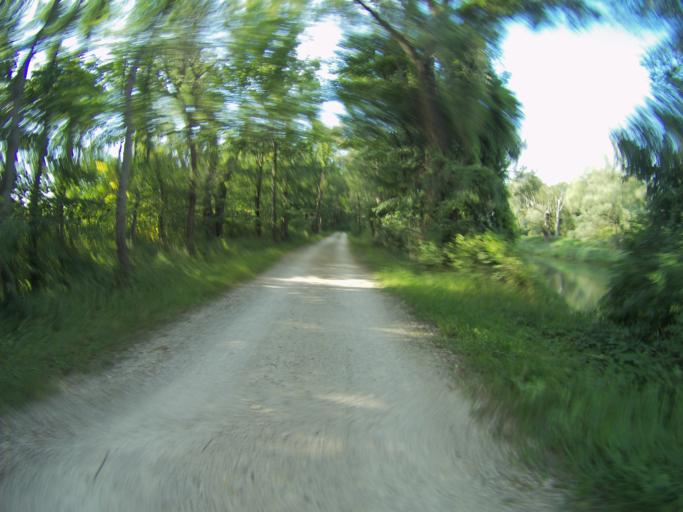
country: DE
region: Bavaria
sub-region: Upper Bavaria
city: Hallbergmoos
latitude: 48.3415
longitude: 11.7123
